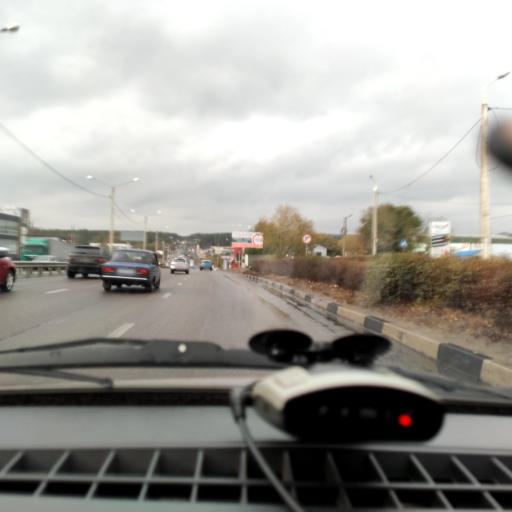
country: RU
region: Voronezj
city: Pridonskoy
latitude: 51.6675
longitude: 39.1262
